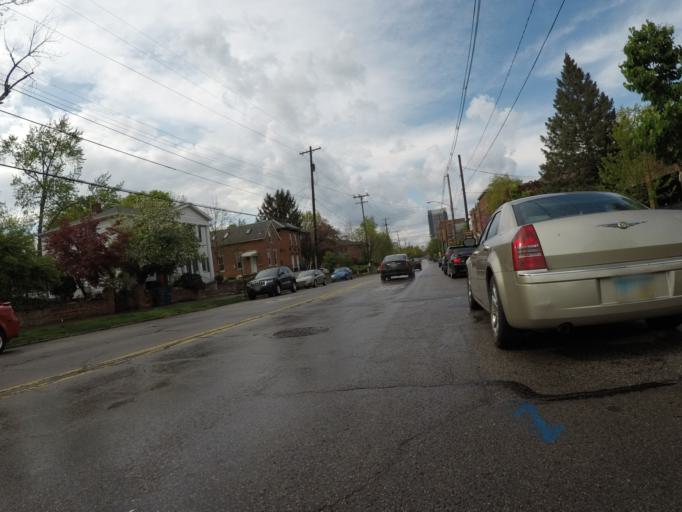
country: US
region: Ohio
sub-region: Franklin County
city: Columbus
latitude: 39.9427
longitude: -82.9986
